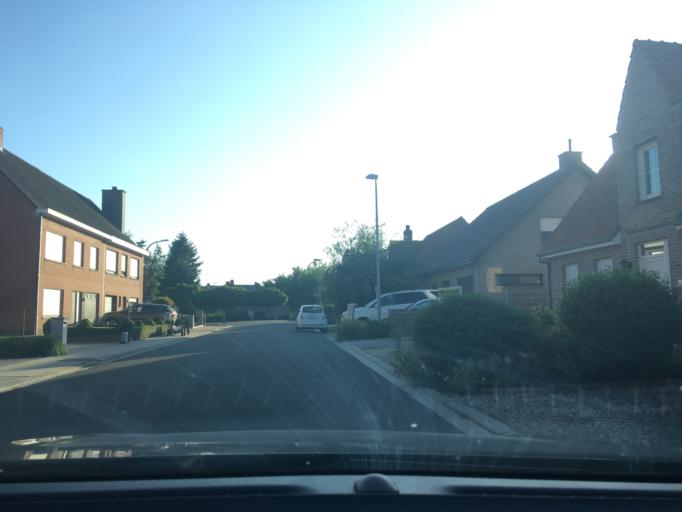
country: BE
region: Flanders
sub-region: Provincie West-Vlaanderen
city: Hooglede
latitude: 50.9990
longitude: 3.1095
